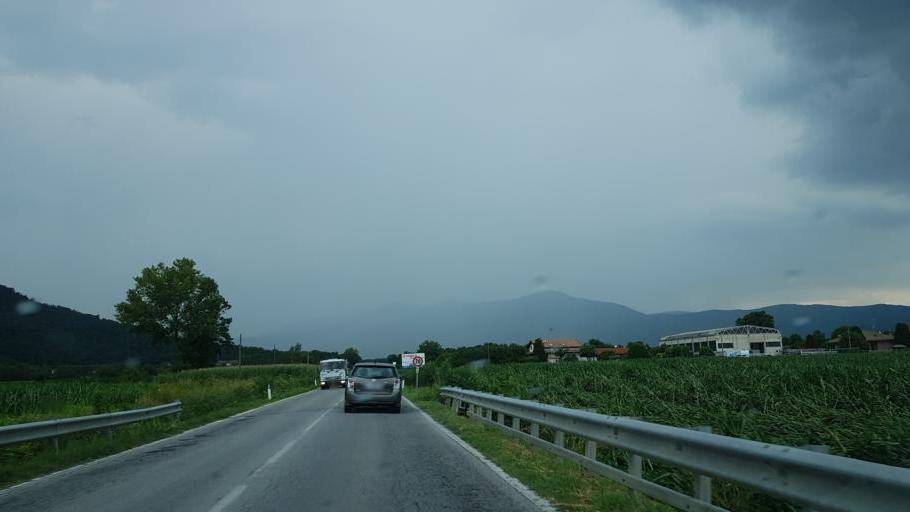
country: IT
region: Piedmont
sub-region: Provincia di Cuneo
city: Caraglio
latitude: 44.4341
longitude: 7.4206
